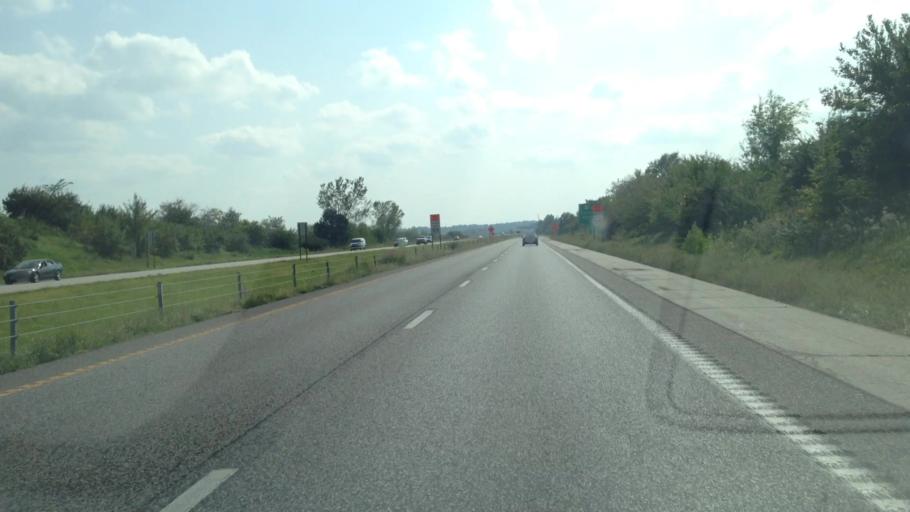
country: US
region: Missouri
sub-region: Clay County
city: Liberty
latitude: 39.2945
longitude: -94.4119
